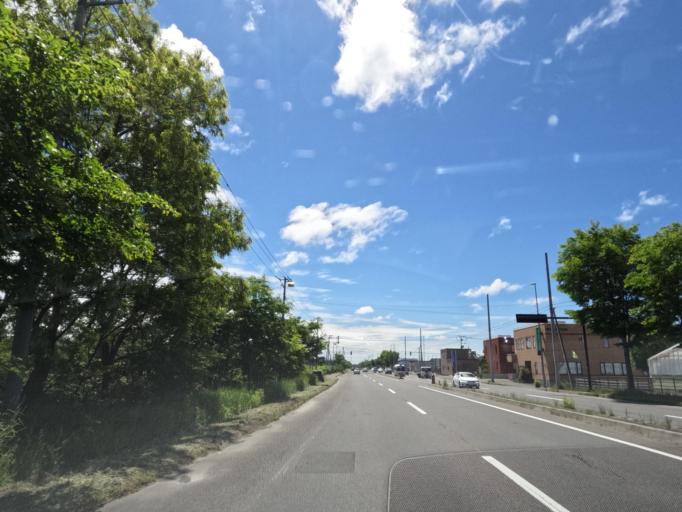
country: JP
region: Hokkaido
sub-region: Asahikawa-shi
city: Asahikawa
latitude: 43.7433
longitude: 142.3585
